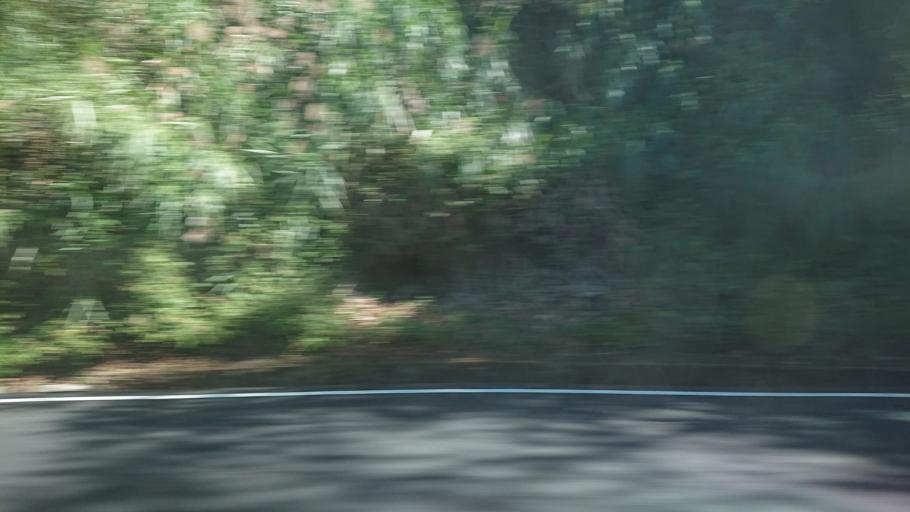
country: TW
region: Taiwan
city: Lugu
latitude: 23.4876
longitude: 120.8225
